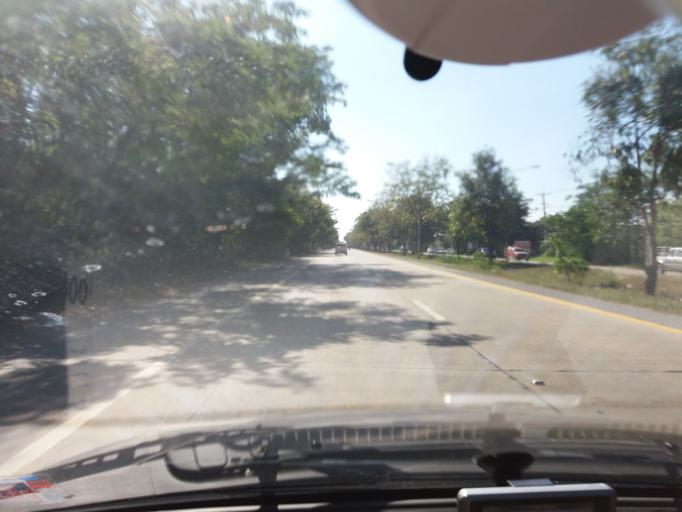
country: TH
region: Suphan Buri
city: Sam Chuk
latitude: 14.7779
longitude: 100.0899
